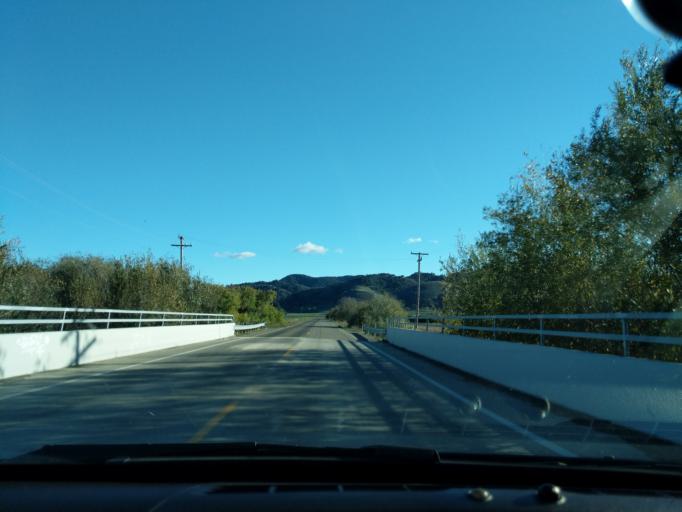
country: US
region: California
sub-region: Santa Barbara County
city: Los Alamos
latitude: 34.7500
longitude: -120.2914
